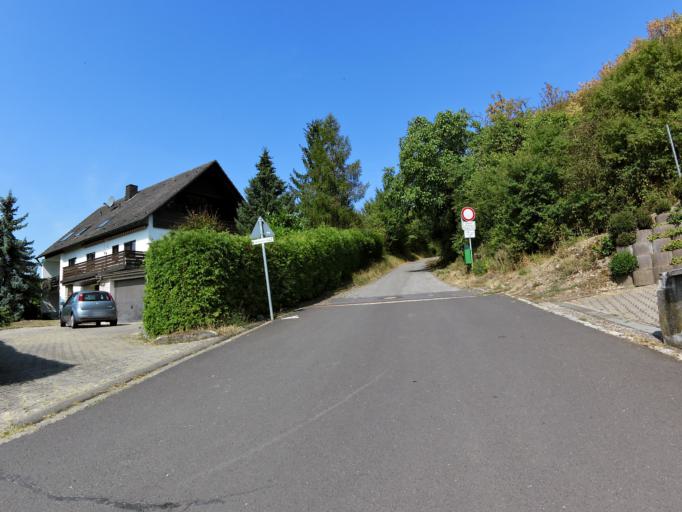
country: DE
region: Bavaria
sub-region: Regierungsbezirk Unterfranken
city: Theilheim
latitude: 49.7555
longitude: 10.0258
